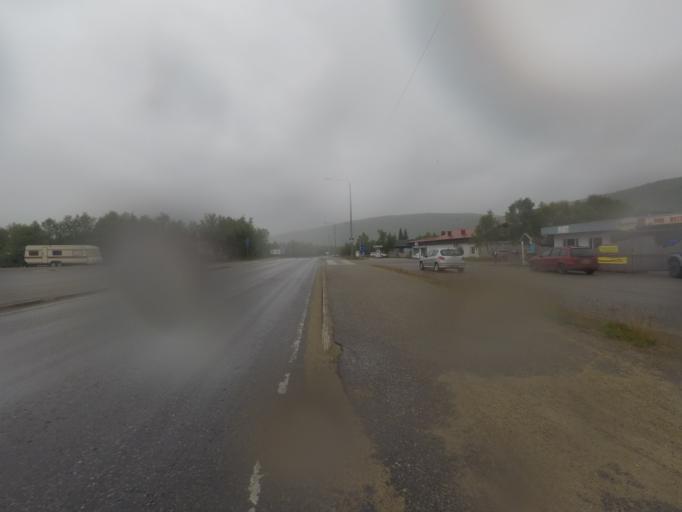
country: FI
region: Lapland
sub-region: Pohjois-Lappi
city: Utsjoki
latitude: 69.9071
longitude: 27.0254
